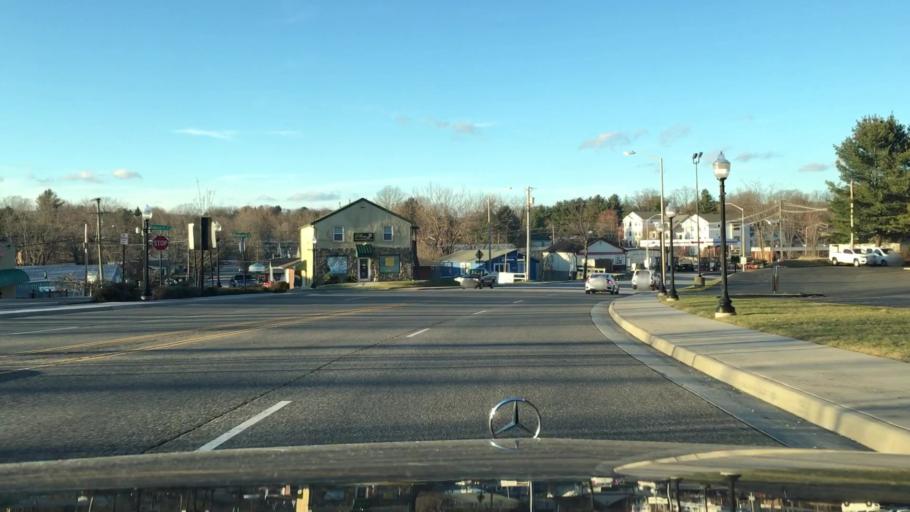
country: US
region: Virginia
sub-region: Montgomery County
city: Blacksburg
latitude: 37.2358
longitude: -80.4210
